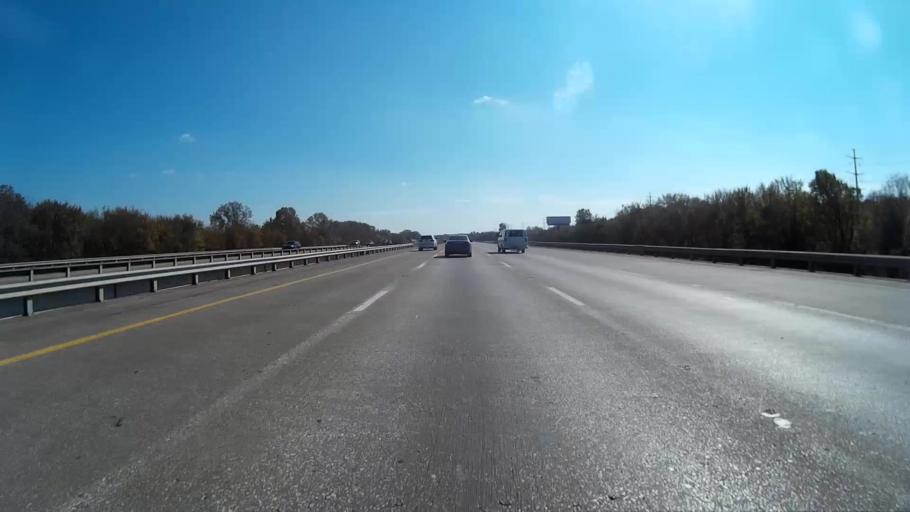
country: US
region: Texas
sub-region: Dallas County
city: Hutchins
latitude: 32.6952
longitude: -96.7509
